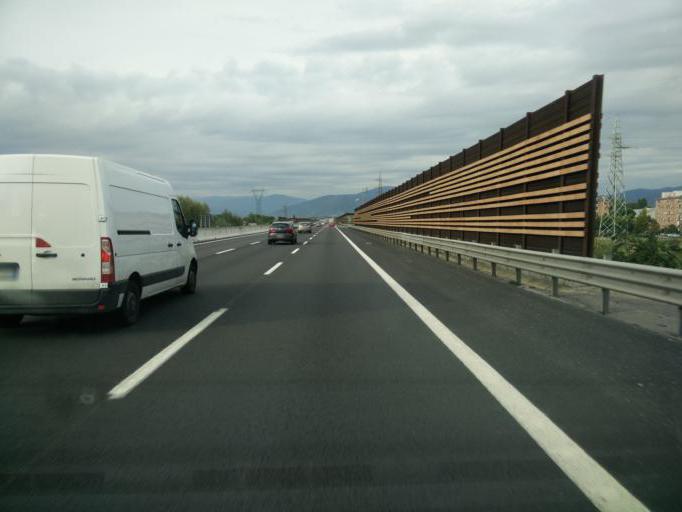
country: IT
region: Tuscany
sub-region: Province of Florence
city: Mantignano-Ugnano
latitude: 43.7887
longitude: 11.1584
